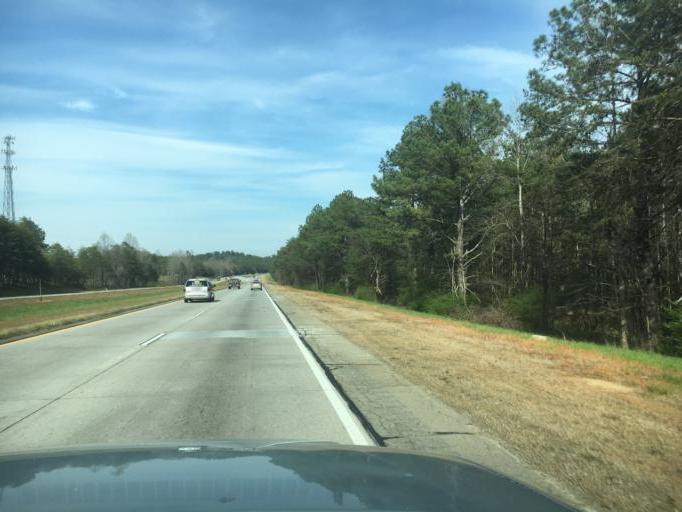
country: US
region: Georgia
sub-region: Hall County
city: Lula
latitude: 34.3707
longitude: -83.7295
